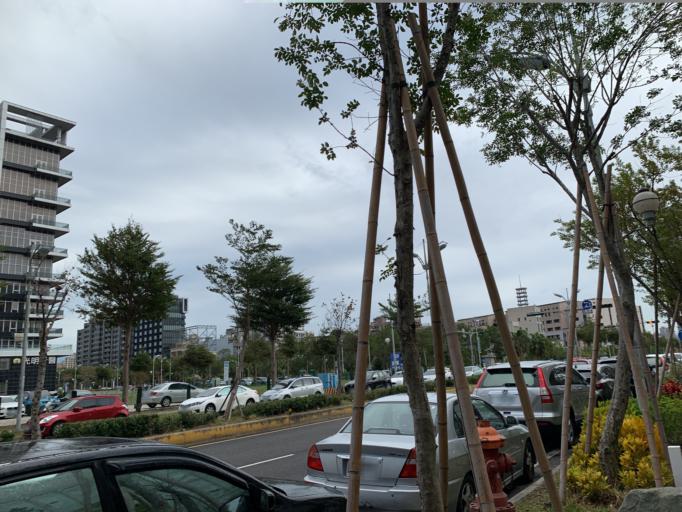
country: TW
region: Taiwan
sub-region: Hsinchu
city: Zhubei
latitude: 24.8158
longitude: 121.0197
